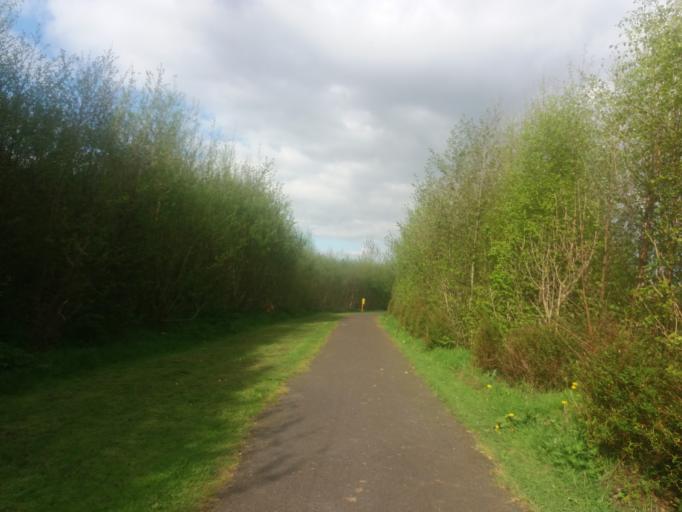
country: IE
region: Leinster
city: Castleknock
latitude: 53.3789
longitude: -6.3298
